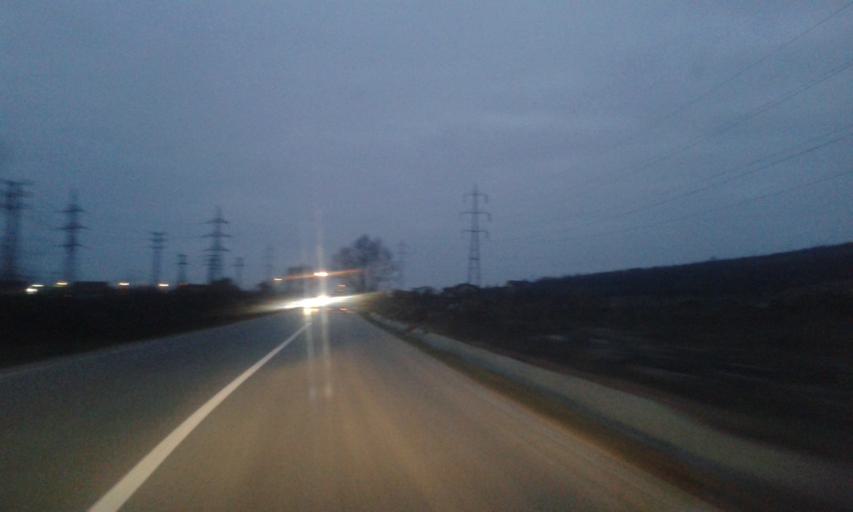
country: RO
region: Gorj
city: Targu Jiu
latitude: 45.0548
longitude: 23.2643
